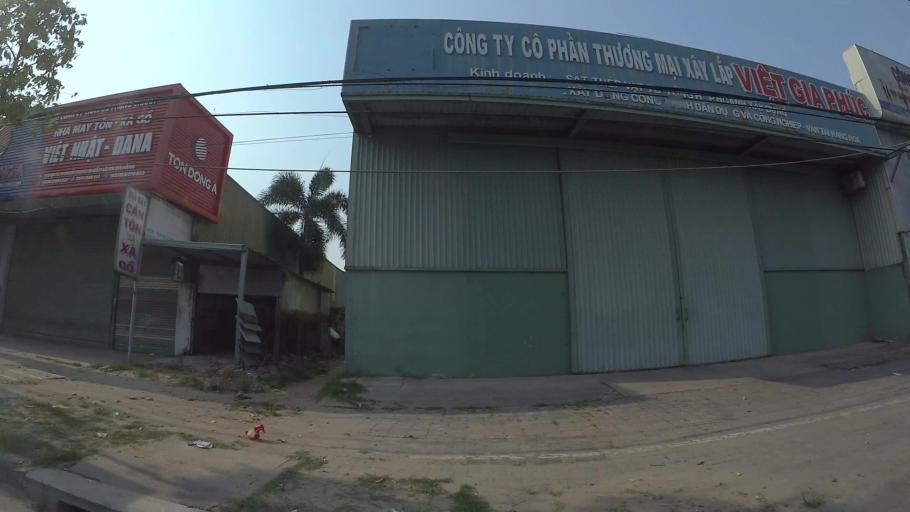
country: VN
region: Da Nang
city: Cam Le
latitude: 16.0196
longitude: 108.2099
